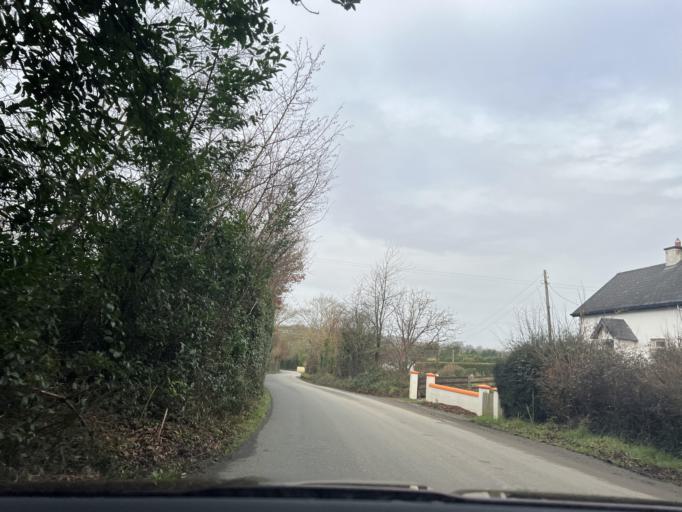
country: IE
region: Leinster
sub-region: Loch Garman
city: Castlebridge
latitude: 52.3821
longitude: -6.5589
